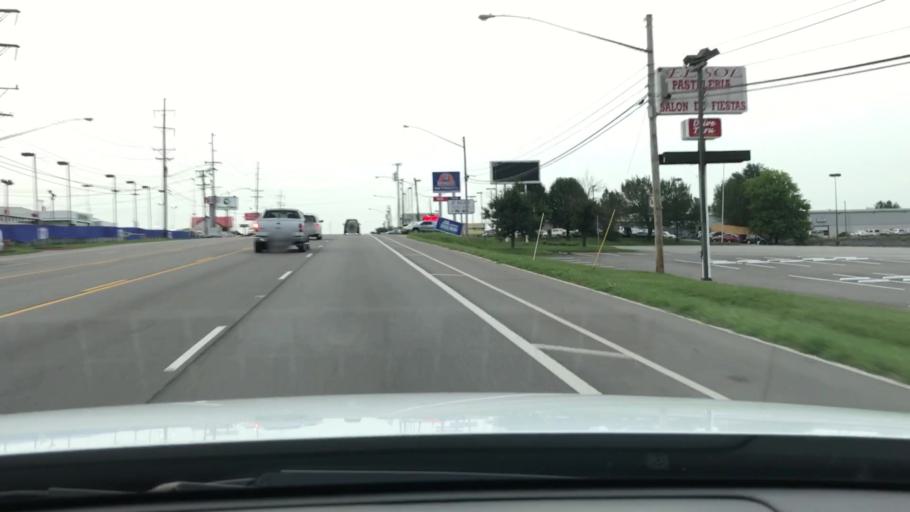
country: US
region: Tennessee
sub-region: Davidson County
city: Goodlettsville
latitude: 36.2874
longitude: -86.7050
